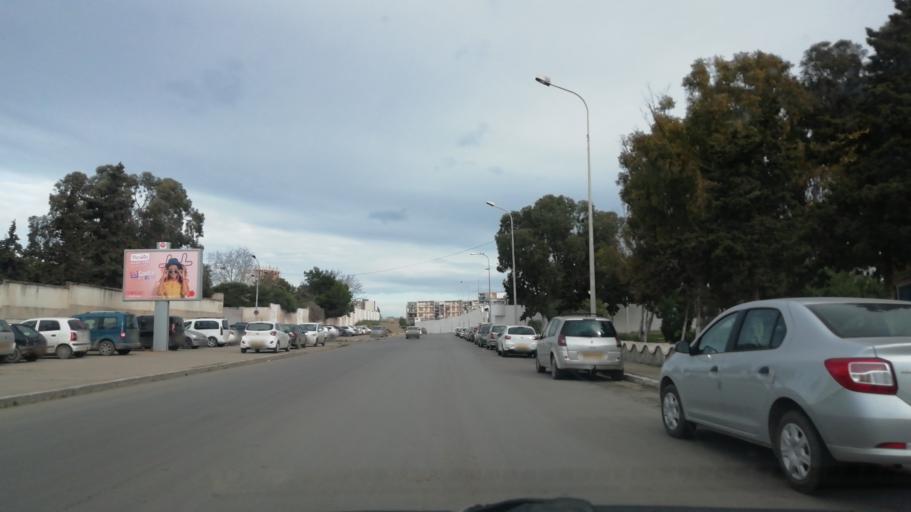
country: DZ
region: Oran
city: Oran
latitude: 35.6983
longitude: -0.6133
